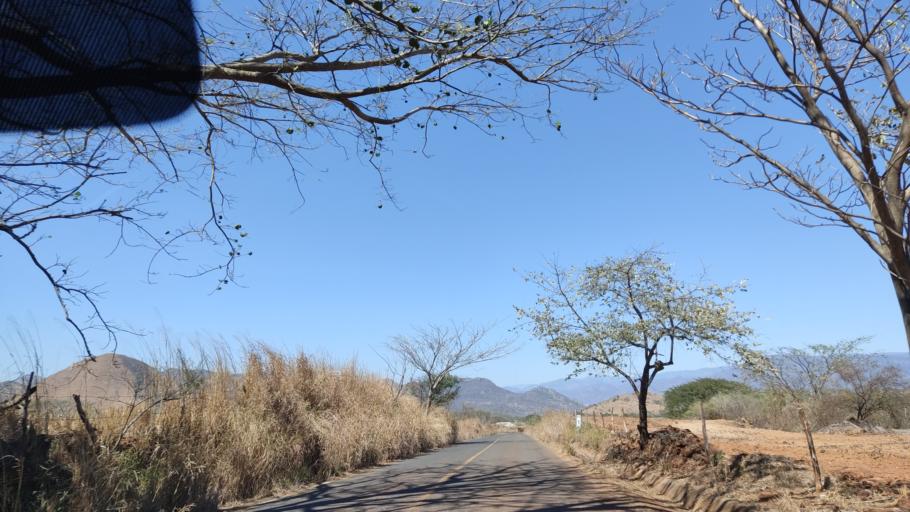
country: MX
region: Nayarit
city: Santa Maria del Oro
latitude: 21.4879
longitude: -104.6244
